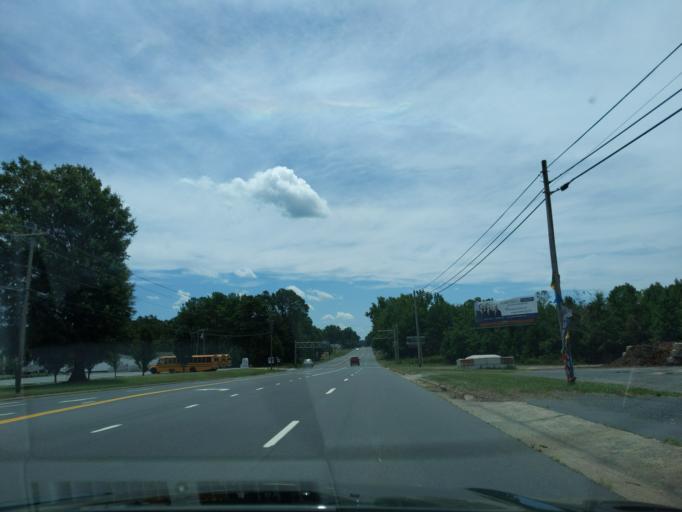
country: US
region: North Carolina
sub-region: Stanly County
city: Albemarle
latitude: 35.4271
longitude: -80.2137
